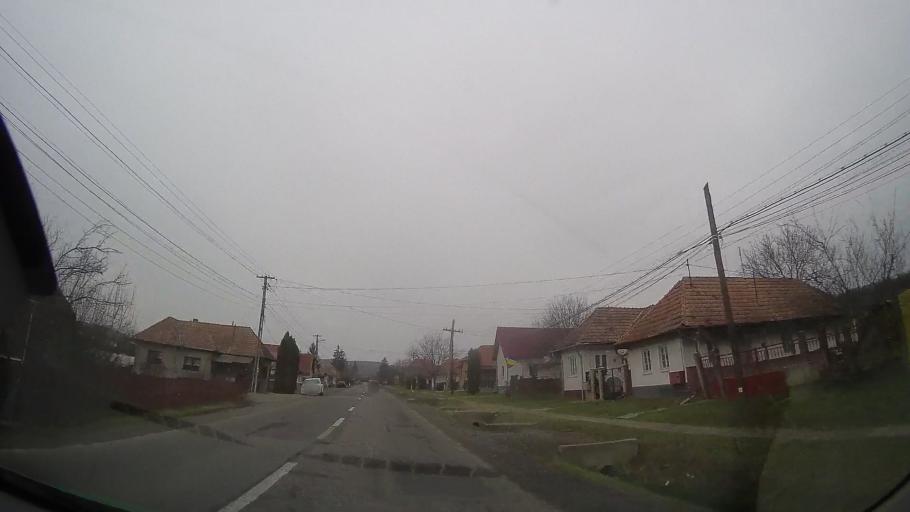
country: RO
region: Mures
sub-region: Comuna Ceausu de Campie
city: Ceausu de Campie
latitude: 46.6437
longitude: 24.5030
